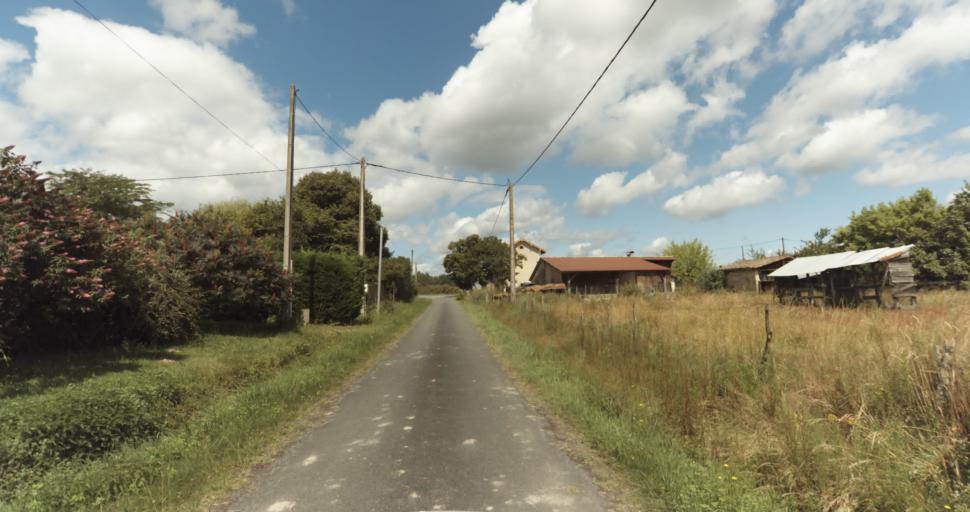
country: FR
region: Aquitaine
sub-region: Departement de la Gironde
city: Bazas
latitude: 44.4625
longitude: -0.1842
